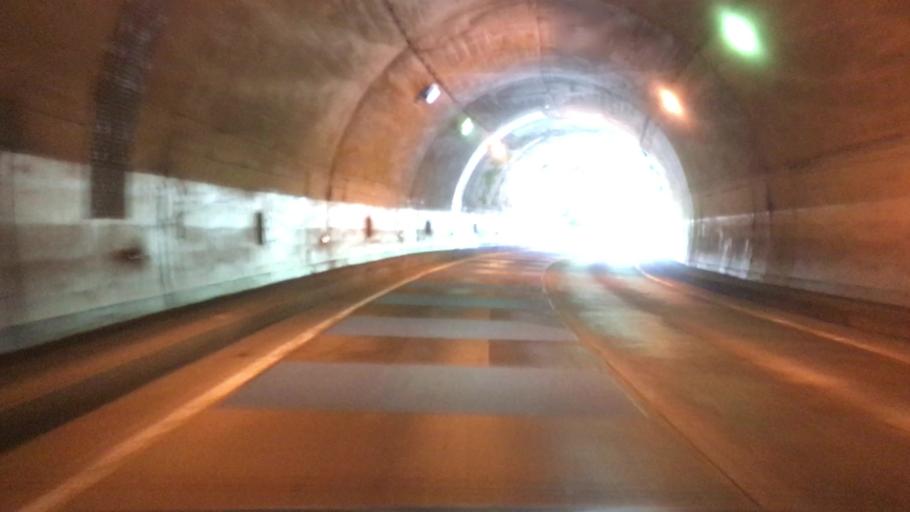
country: JP
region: Tottori
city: Tottori
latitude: 35.5942
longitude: 134.3562
